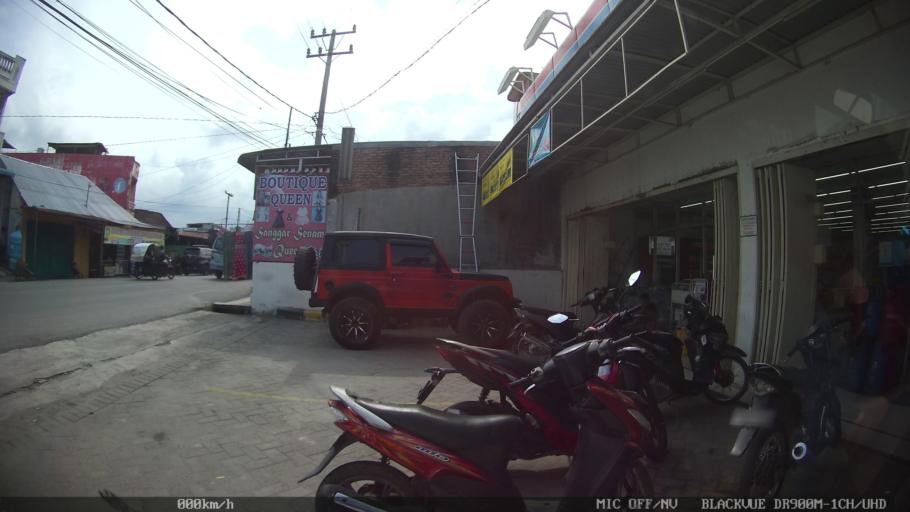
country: ID
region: North Sumatra
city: Medan
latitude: 3.6072
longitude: 98.7583
